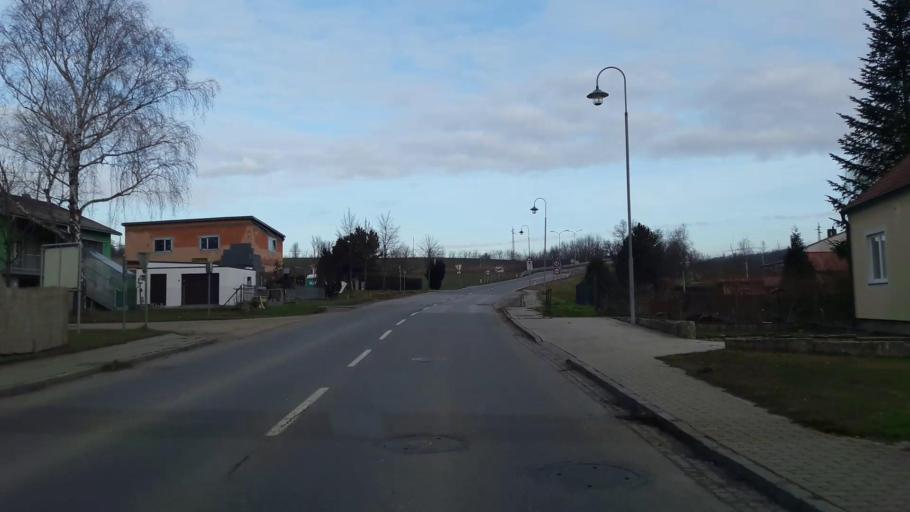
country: AT
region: Lower Austria
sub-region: Politischer Bezirk Mistelbach
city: Staatz
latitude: 48.6307
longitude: 16.5180
